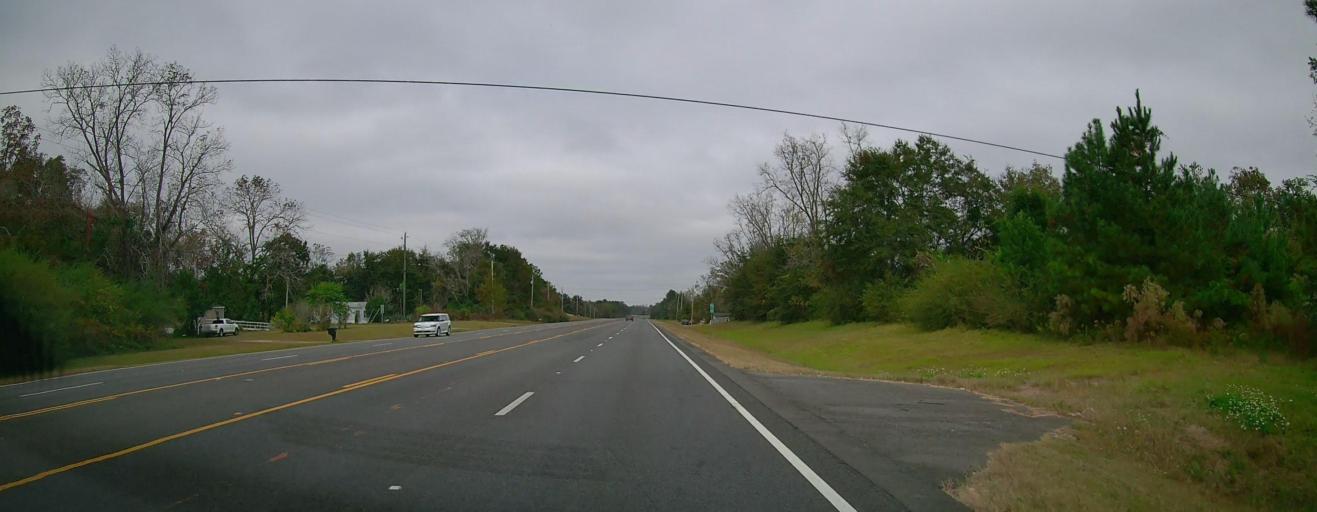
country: US
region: Georgia
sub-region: Thomas County
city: Thomasville
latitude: 30.9271
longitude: -83.9128
